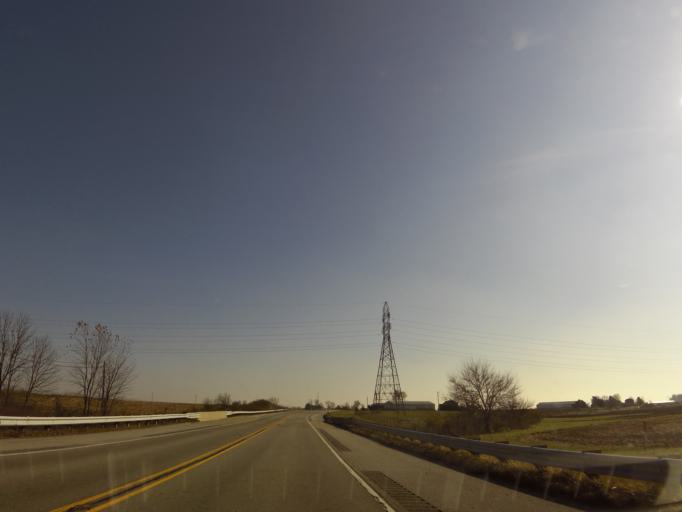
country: US
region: Indiana
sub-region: Union County
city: Liberty
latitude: 39.5871
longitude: -84.8471
